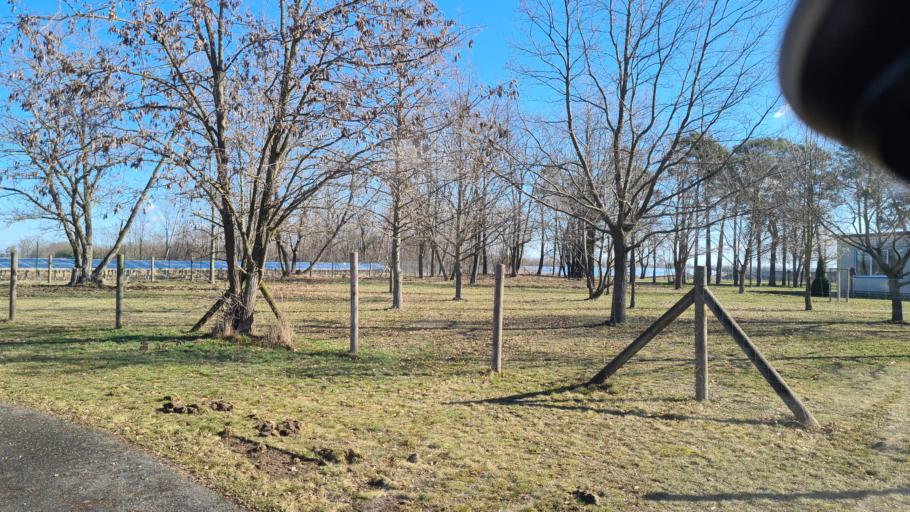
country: DE
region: Brandenburg
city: Falkenberg
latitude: 51.5508
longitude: 13.2168
